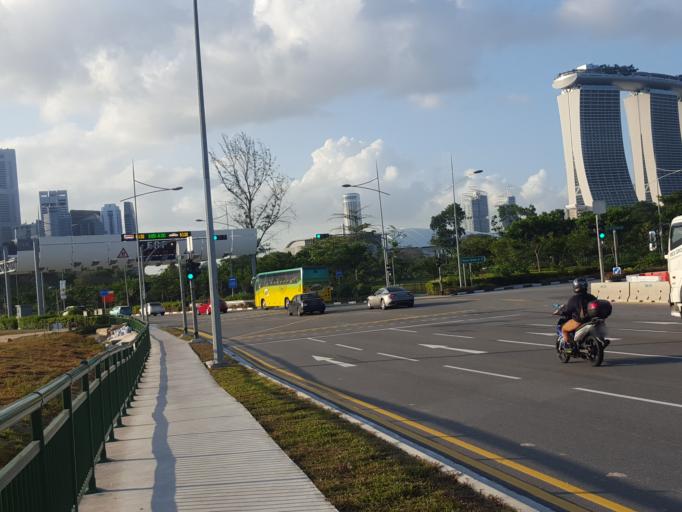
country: SG
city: Singapore
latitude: 1.2737
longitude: 103.8612
